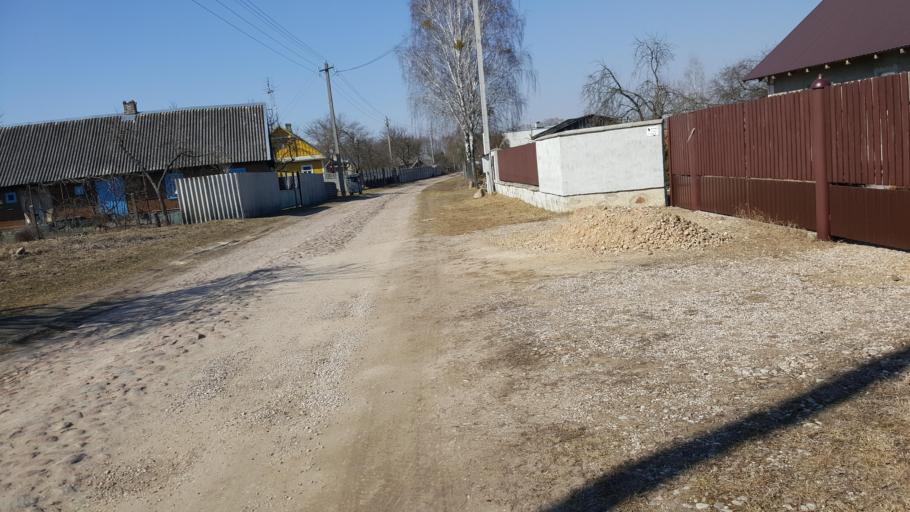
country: BY
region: Brest
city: Kamyanyets
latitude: 52.3558
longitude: 23.7513
